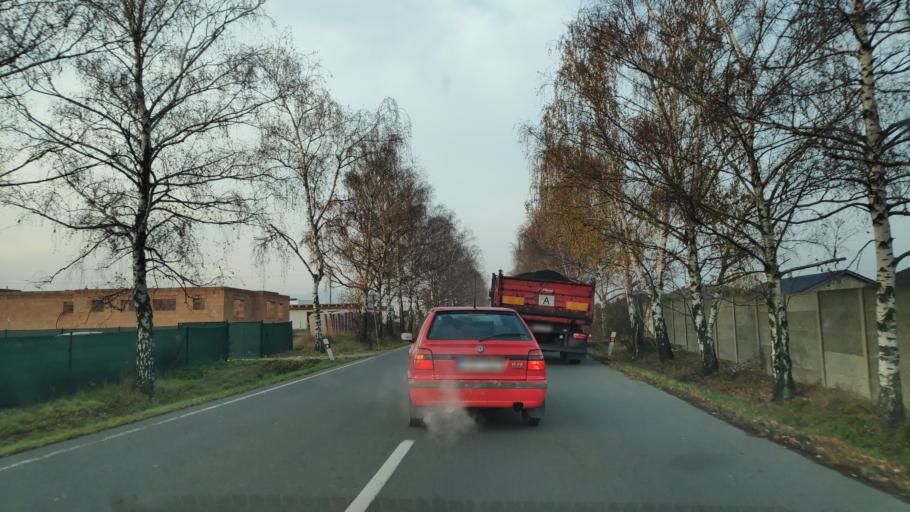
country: CZ
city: Sviadnov
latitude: 49.6942
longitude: 18.3194
